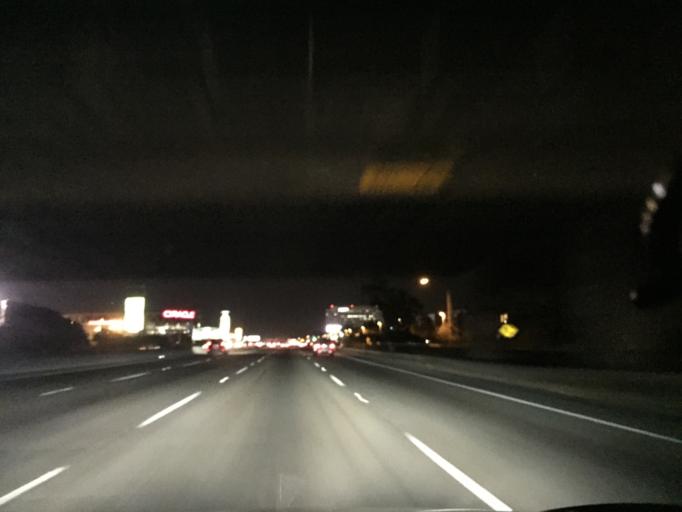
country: US
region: California
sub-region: Alameda County
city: Alameda
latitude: 37.7542
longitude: -122.2085
